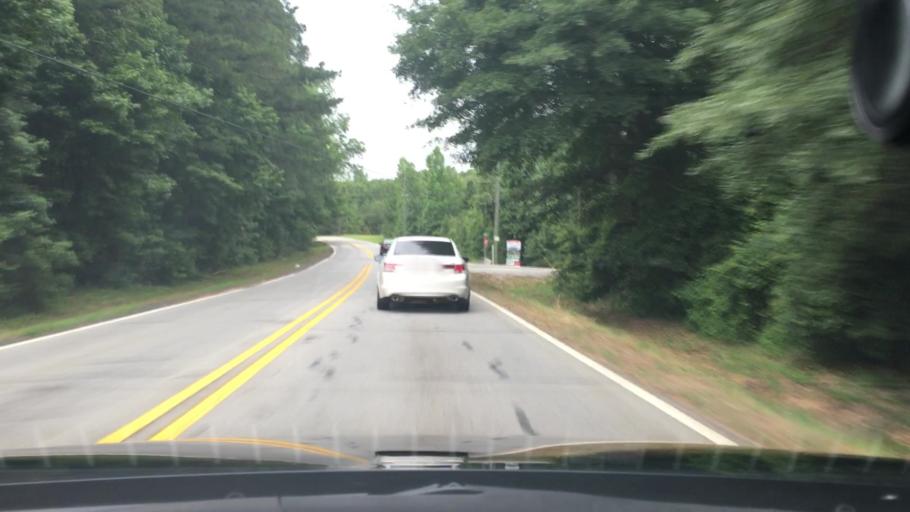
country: US
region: Georgia
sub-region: Coweta County
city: East Newnan
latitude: 33.3540
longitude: -84.7034
